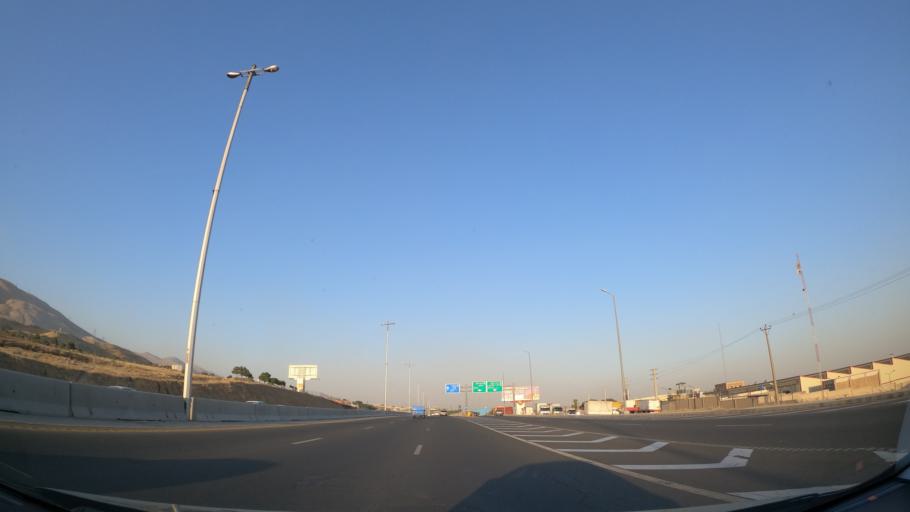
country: IR
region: Tehran
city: Shahr-e Qods
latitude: 35.7425
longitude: 51.1100
